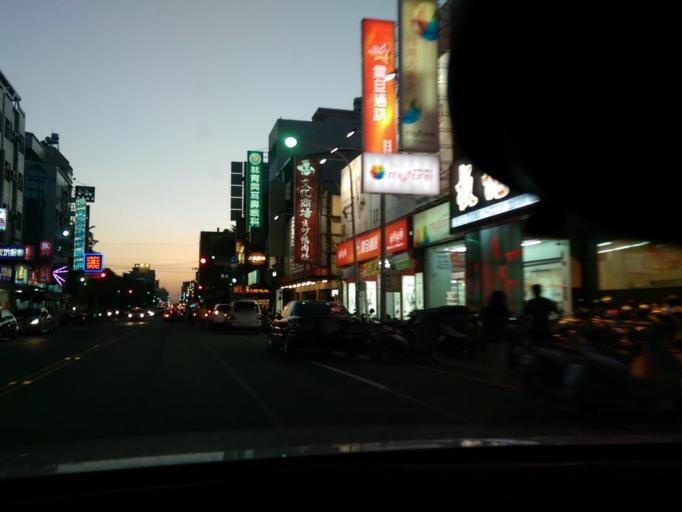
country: TW
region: Taiwan
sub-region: Chiayi
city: Jiayi Shi
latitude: 23.4767
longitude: 120.4574
